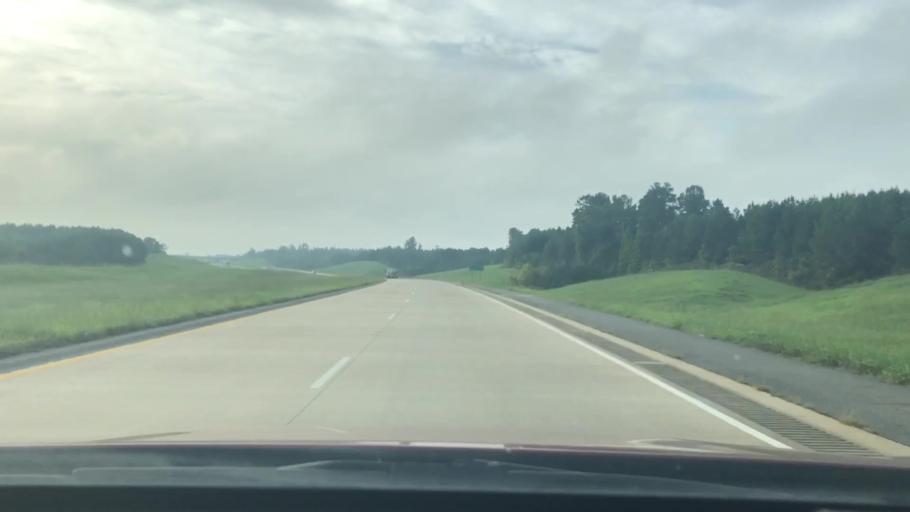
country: US
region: Louisiana
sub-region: Caddo Parish
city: Vivian
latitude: 32.9308
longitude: -93.8954
